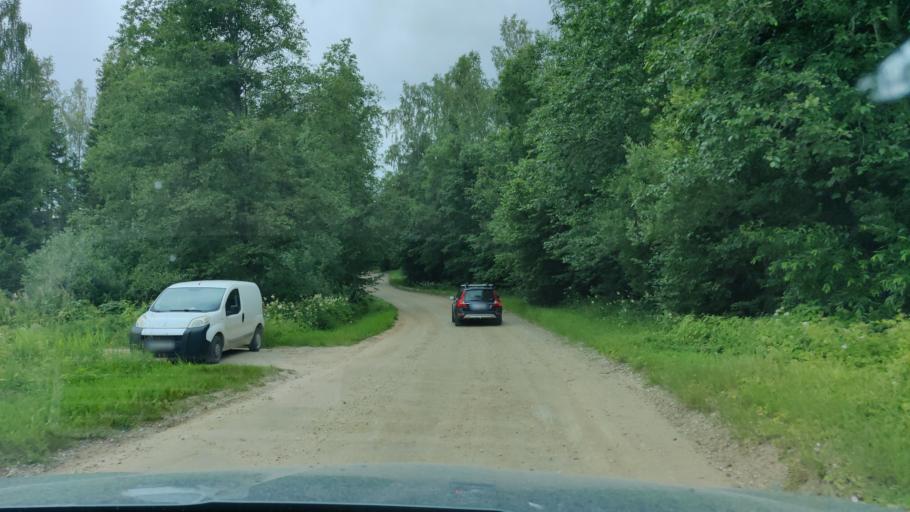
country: EE
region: Vorumaa
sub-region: Antsla vald
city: Vana-Antsla
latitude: 58.0324
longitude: 26.5512
